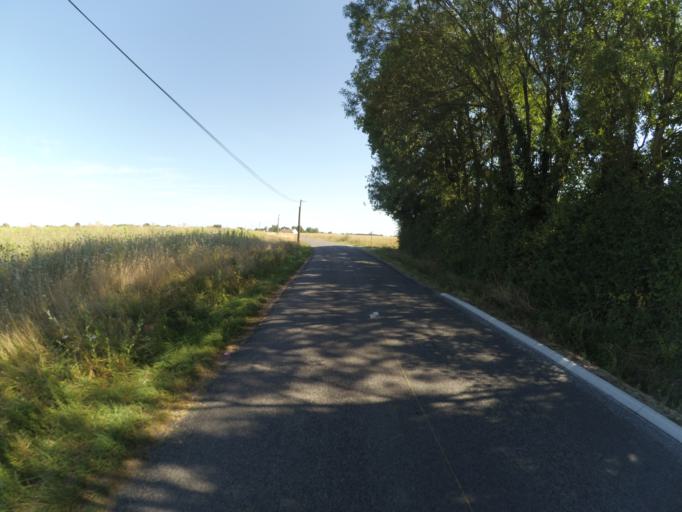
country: FR
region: Pays de la Loire
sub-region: Departement de la Loire-Atlantique
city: La Chapelle-Heulin
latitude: 47.1623
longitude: -1.3335
